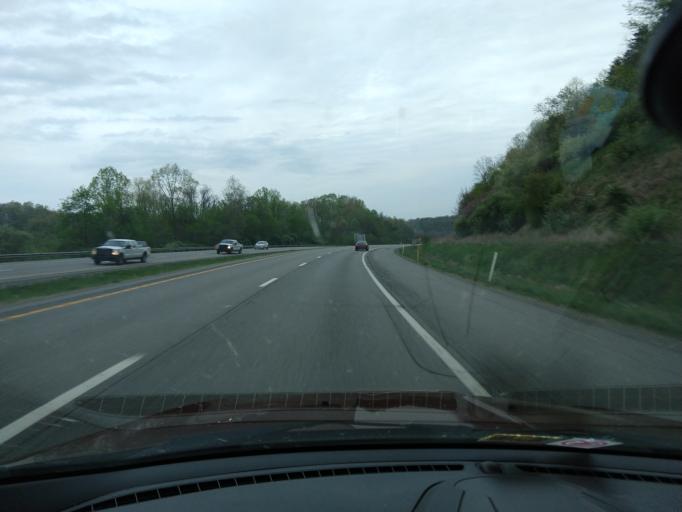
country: US
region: West Virginia
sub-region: Lewis County
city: Weston
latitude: 39.0486
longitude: -80.4080
